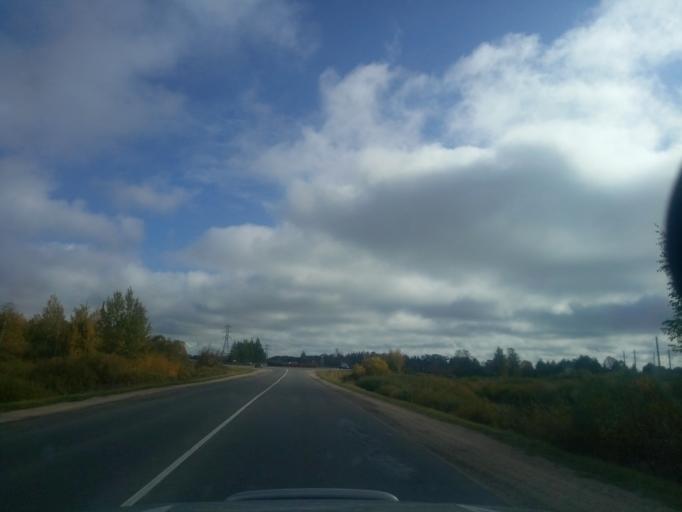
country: BY
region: Minsk
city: Zaslawye
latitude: 54.0014
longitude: 27.2736
